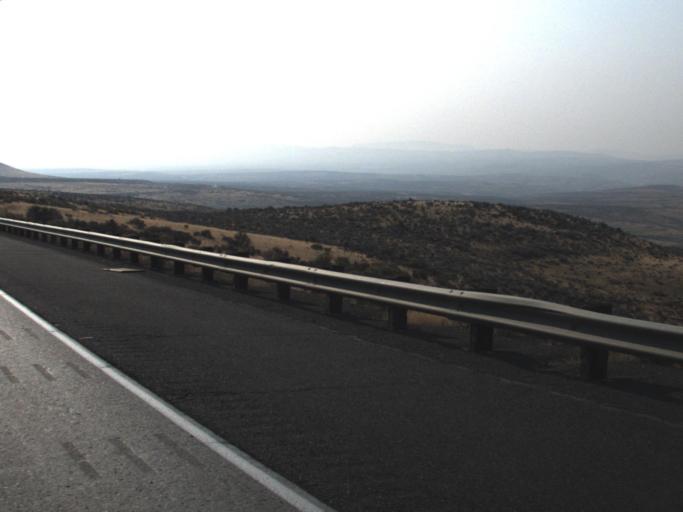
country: US
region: Washington
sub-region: Kittitas County
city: Kittitas
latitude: 46.8667
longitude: -120.4104
